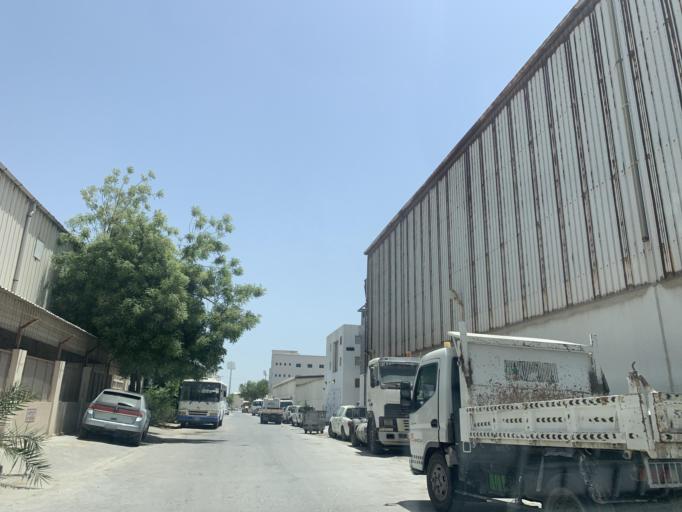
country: BH
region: Northern
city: Sitrah
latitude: 26.1540
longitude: 50.6218
